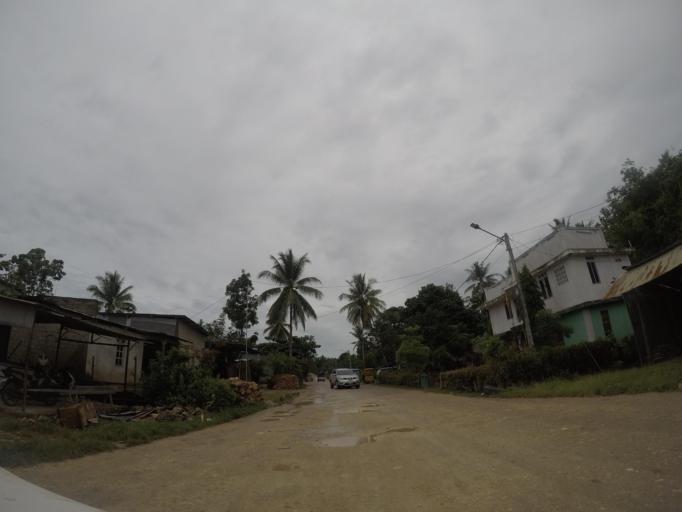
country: TL
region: Lautem
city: Lospalos
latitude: -8.5153
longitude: 127.0016
